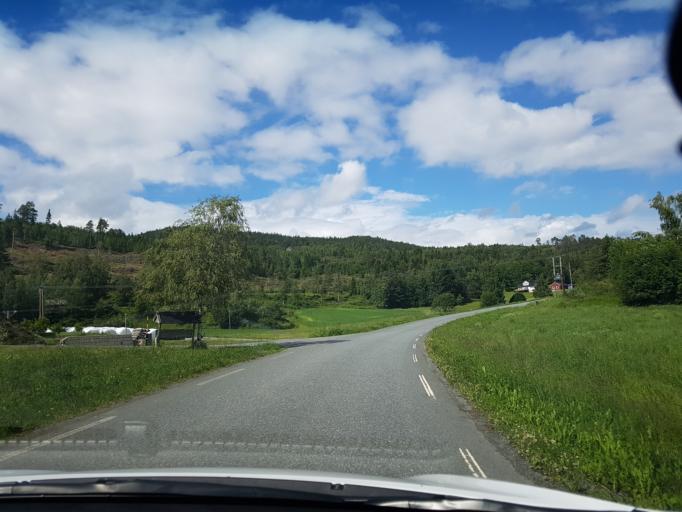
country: NO
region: Nord-Trondelag
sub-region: Frosta
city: Frosta
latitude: 63.6001
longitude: 10.8399
